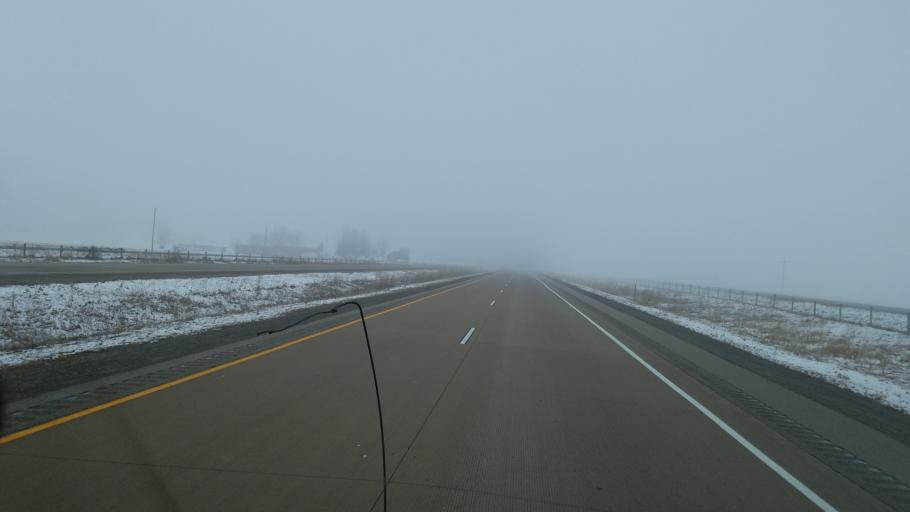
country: US
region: Wisconsin
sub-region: Winnebago County
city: Winneconne
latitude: 44.1730
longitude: -88.6643
